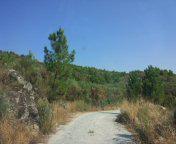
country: PT
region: Viseu
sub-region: Sernancelhe
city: Sernancelhe
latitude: 40.9312
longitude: -7.5166
